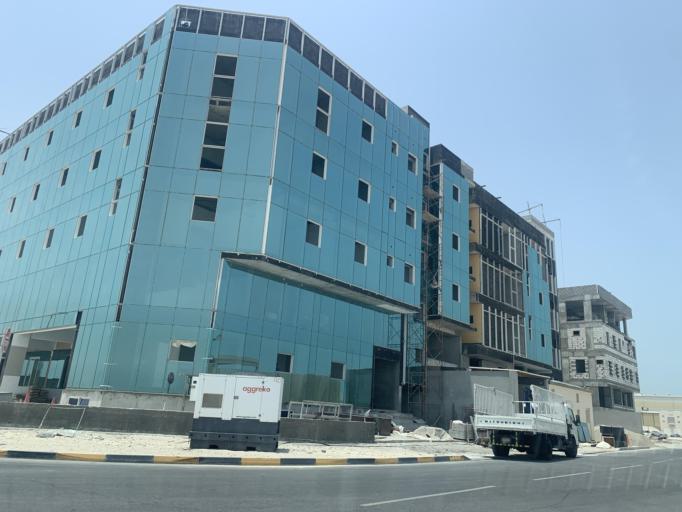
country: BH
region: Muharraq
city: Al Hadd
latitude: 26.2546
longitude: 50.6708
